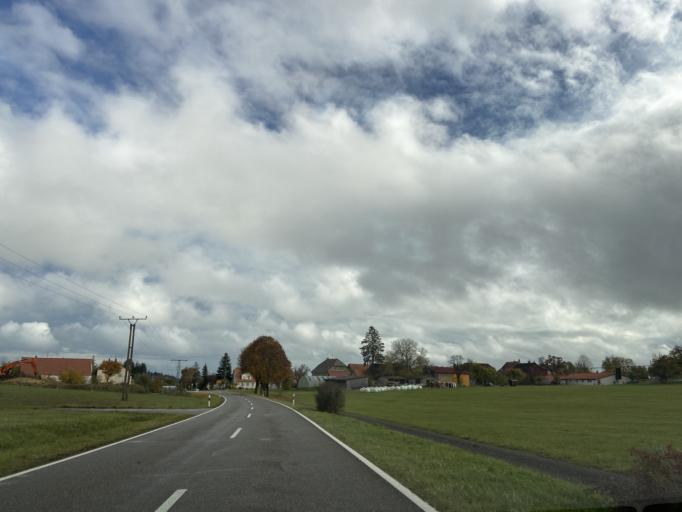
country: DE
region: Baden-Wuerttemberg
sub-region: Tuebingen Region
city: Messkirch
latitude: 48.0468
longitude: 9.1002
